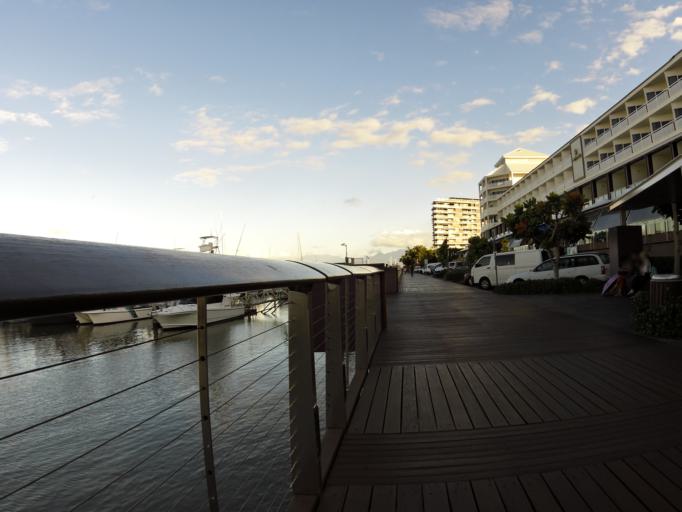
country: AU
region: Queensland
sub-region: Cairns
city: Cairns
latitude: -16.9192
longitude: 145.7808
